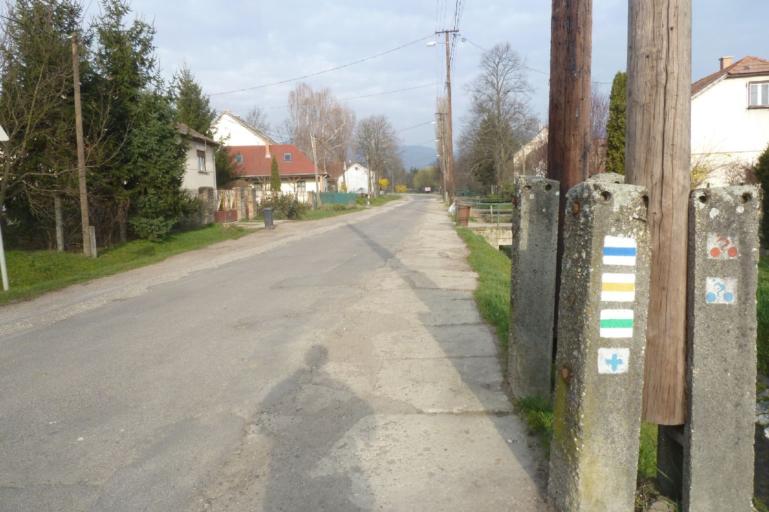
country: HU
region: Nograd
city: Diosjeno
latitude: 47.9415
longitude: 19.0500
